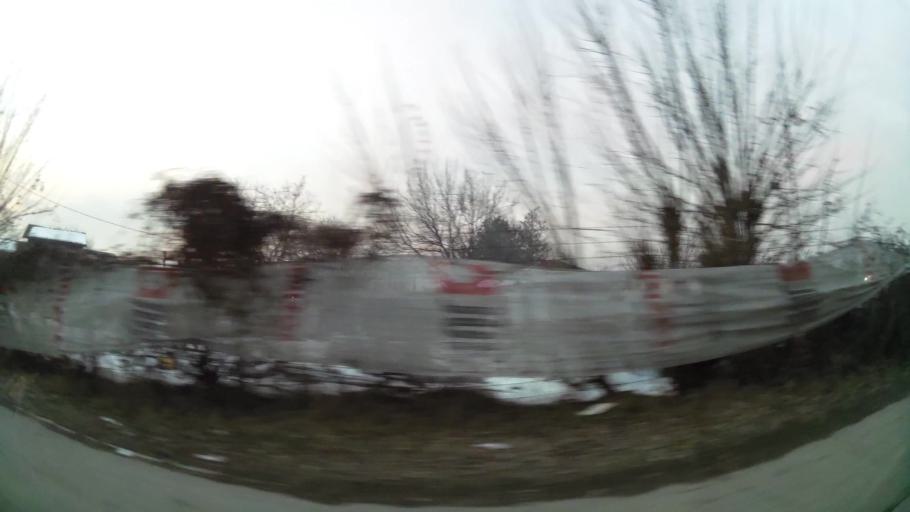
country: MK
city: Krushopek
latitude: 42.0125
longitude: 21.3801
